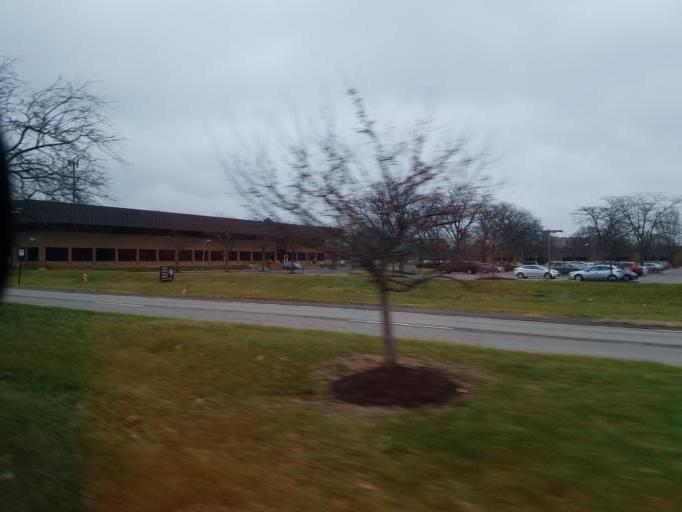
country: US
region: Ohio
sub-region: Franklin County
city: Worthington
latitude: 40.0988
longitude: -82.9935
